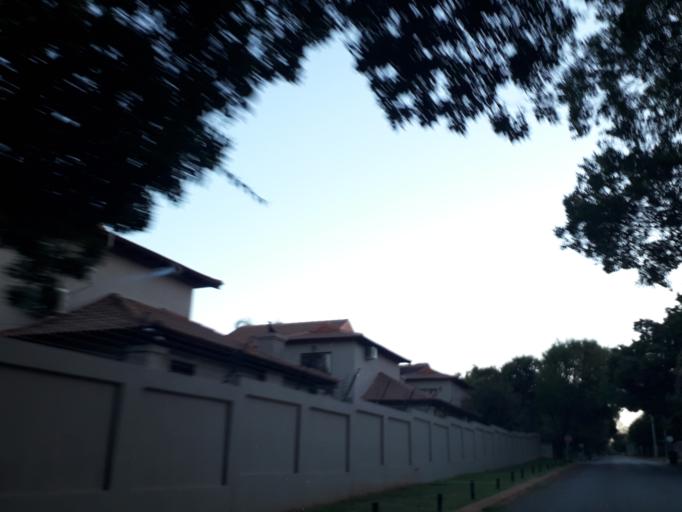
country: ZA
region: Gauteng
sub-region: City of Johannesburg Metropolitan Municipality
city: Roodepoort
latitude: -26.1274
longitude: 27.9447
